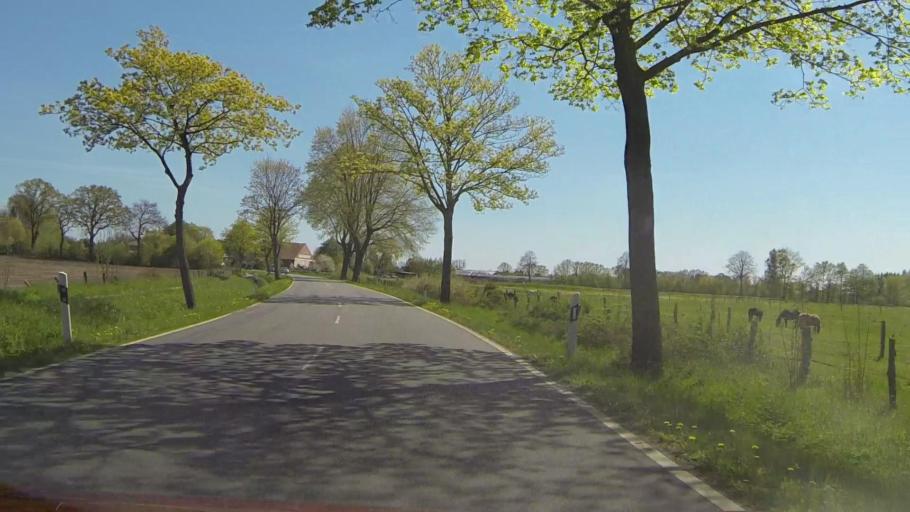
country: DE
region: Schleswig-Holstein
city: Ellerbek
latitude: 53.6513
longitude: 9.8702
